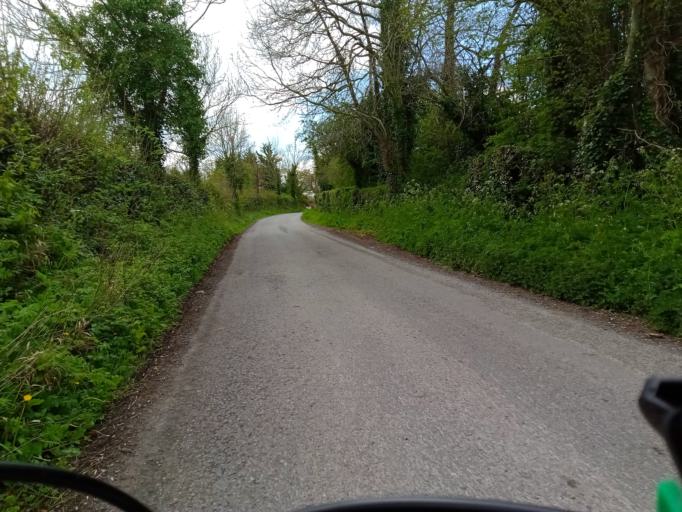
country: IE
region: Leinster
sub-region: Kilkenny
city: Kilkenny
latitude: 52.6317
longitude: -7.2842
